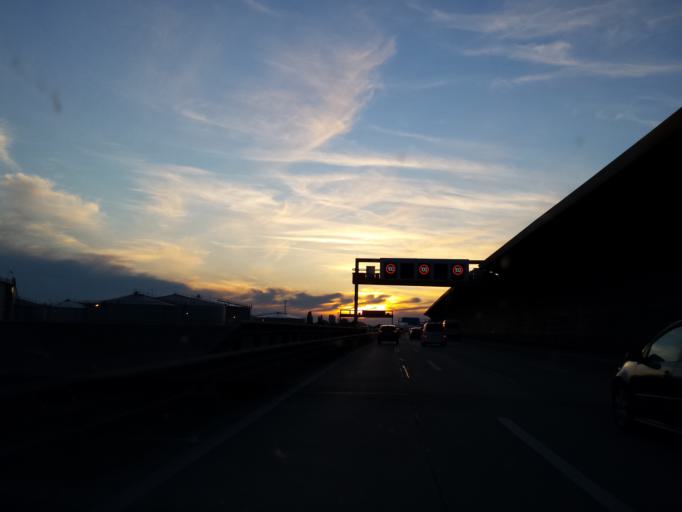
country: AT
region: Lower Austria
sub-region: Politischer Bezirk Wien-Umgebung
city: Schwechat
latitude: 48.1467
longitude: 16.5025
